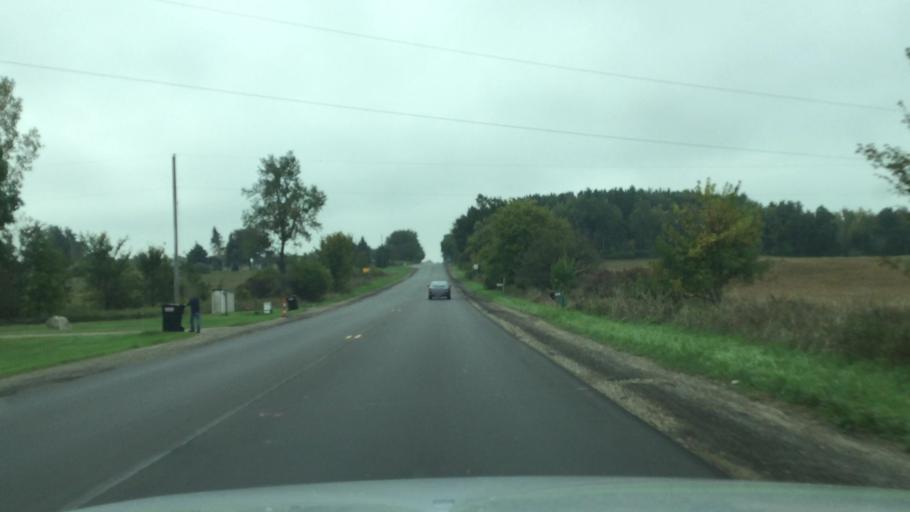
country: US
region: Michigan
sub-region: Shiawassee County
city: Perry
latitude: 42.8518
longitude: -84.2204
